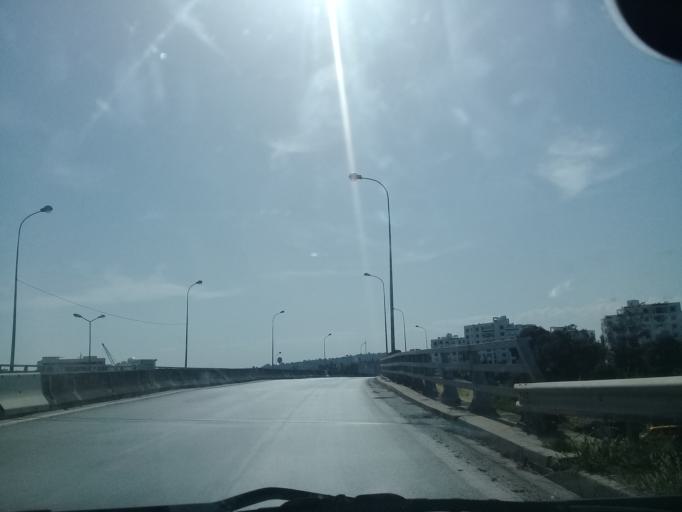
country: TN
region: Tunis
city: Tunis
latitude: 36.8248
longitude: 10.2004
